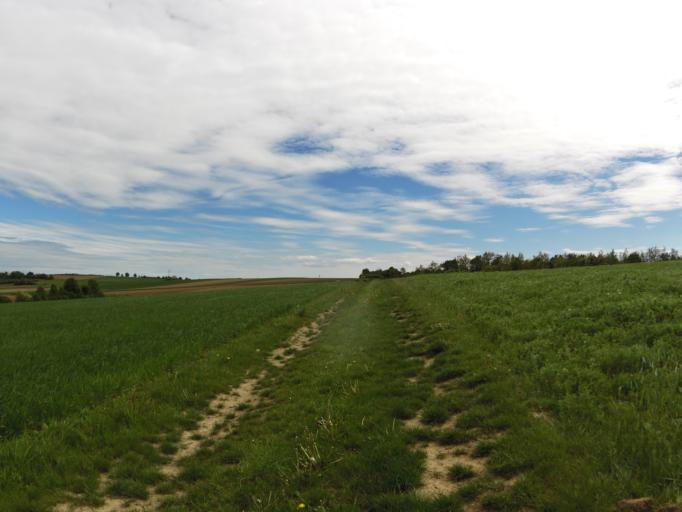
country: DE
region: Bavaria
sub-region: Regierungsbezirk Unterfranken
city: Kurnach
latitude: 49.8409
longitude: 10.0297
